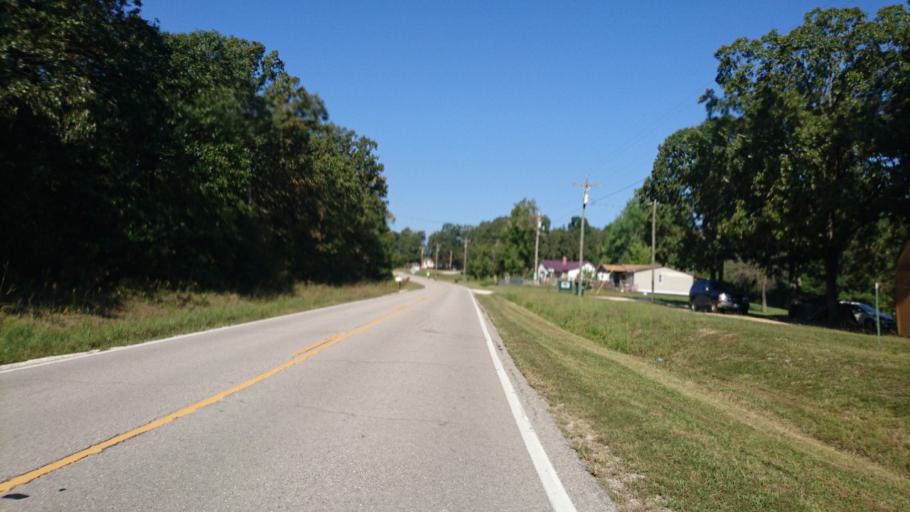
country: US
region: Missouri
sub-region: Pulaski County
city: Richland
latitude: 37.7664
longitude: -92.4009
